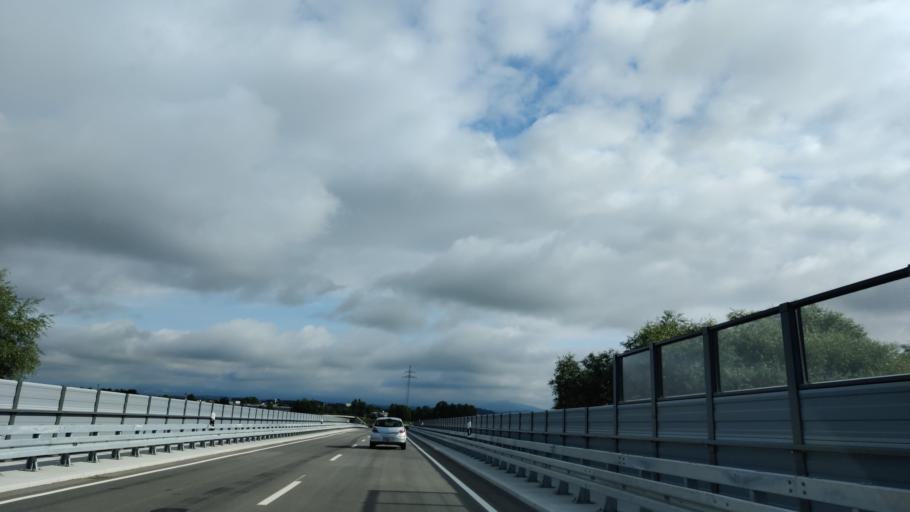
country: DE
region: Bavaria
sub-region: Lower Bavaria
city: Plattling
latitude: 48.7793
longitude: 12.8971
